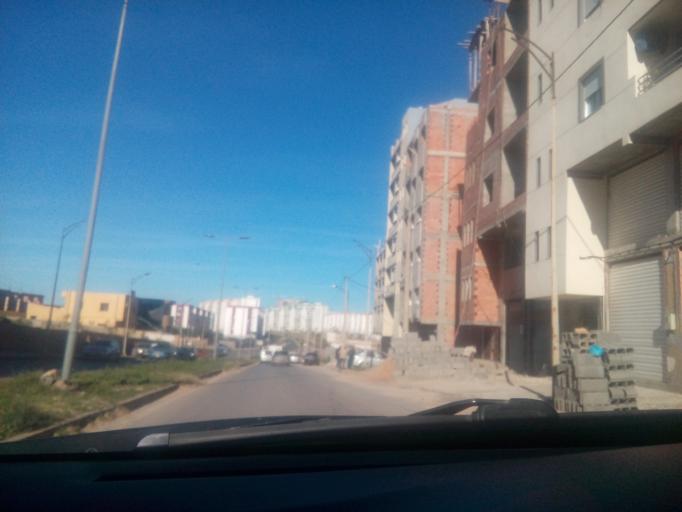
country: DZ
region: Oran
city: Bir el Djir
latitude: 35.7495
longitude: -0.5513
